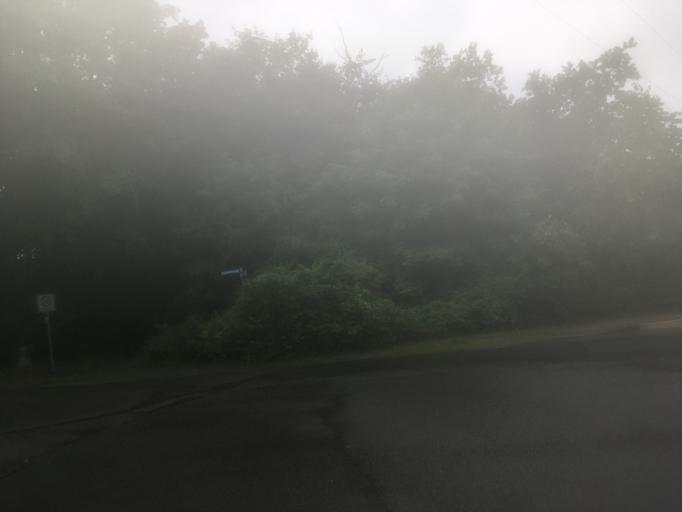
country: DE
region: Brandenburg
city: Zehdenick
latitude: 53.0051
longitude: 13.3471
